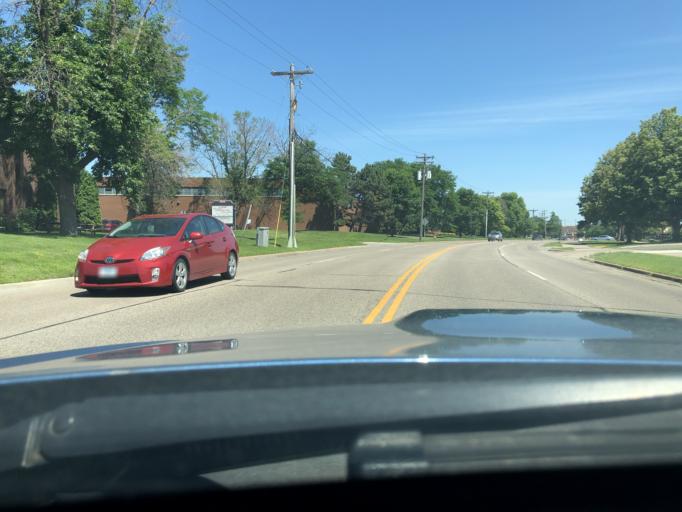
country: US
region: Minnesota
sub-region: Ramsey County
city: Roseville
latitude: 45.0150
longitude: -93.1814
